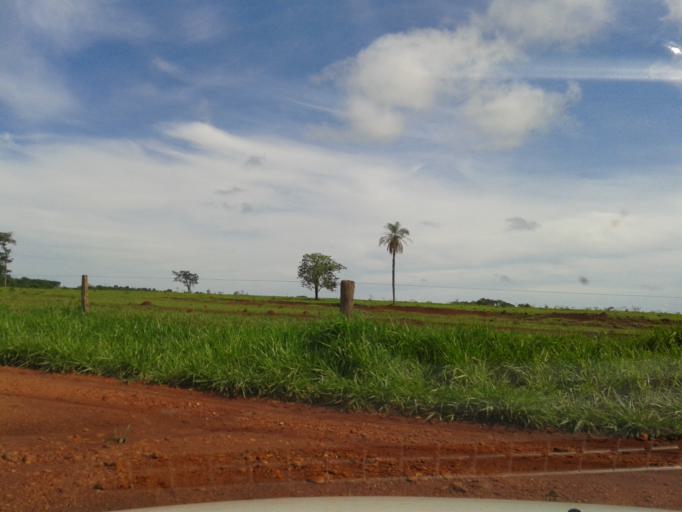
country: BR
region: Minas Gerais
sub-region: Santa Vitoria
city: Santa Vitoria
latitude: -19.2172
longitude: -50.6757
